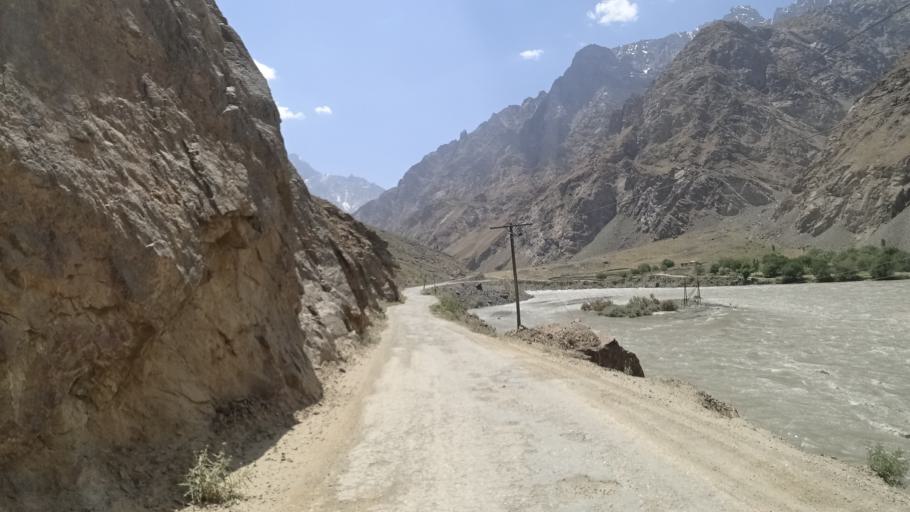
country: TJ
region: Gorno-Badakhshan
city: Rushon
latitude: 37.8483
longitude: 71.5871
